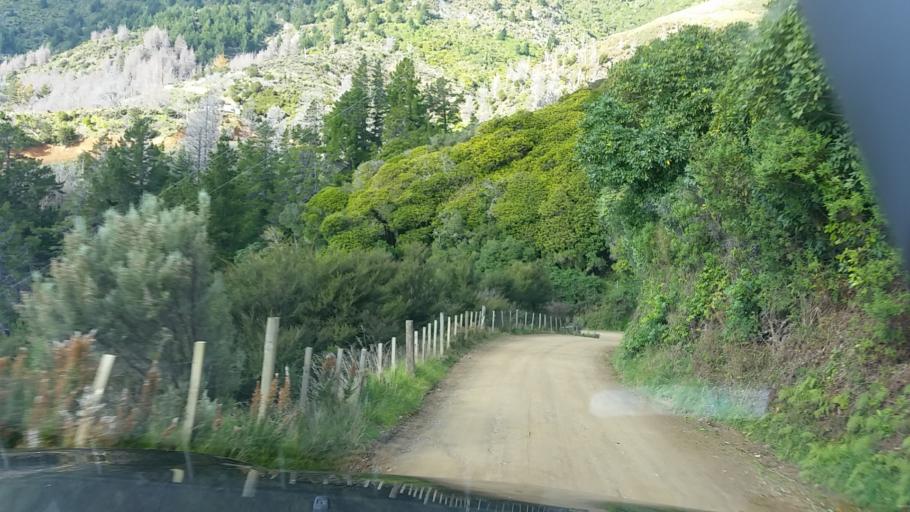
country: NZ
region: Marlborough
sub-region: Marlborough District
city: Picton
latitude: -40.9905
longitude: 173.8456
